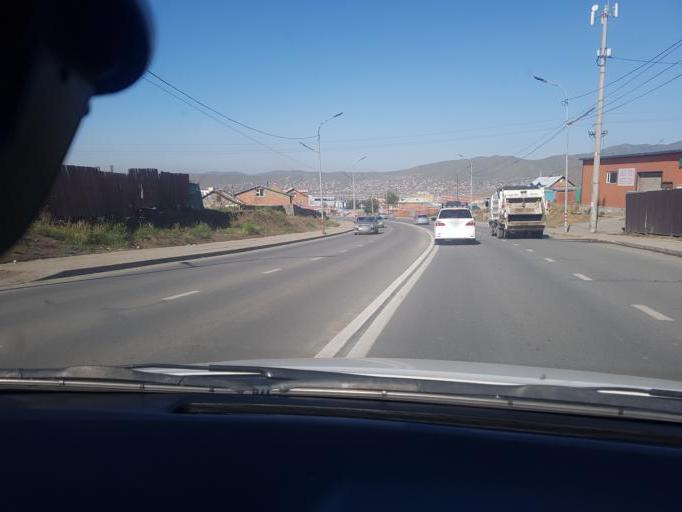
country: MN
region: Ulaanbaatar
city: Ulaanbaatar
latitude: 47.9556
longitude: 106.8466
